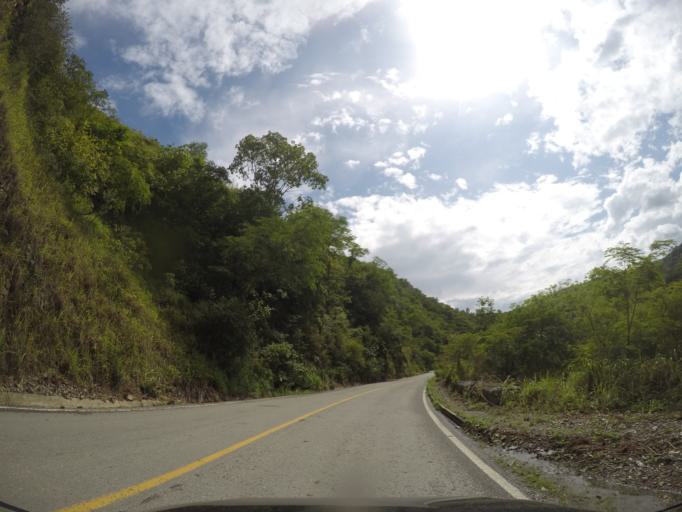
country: MX
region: Oaxaca
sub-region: San Jeronimo Coatlan
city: San Cristobal Honduras
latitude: 16.3710
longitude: -97.0833
